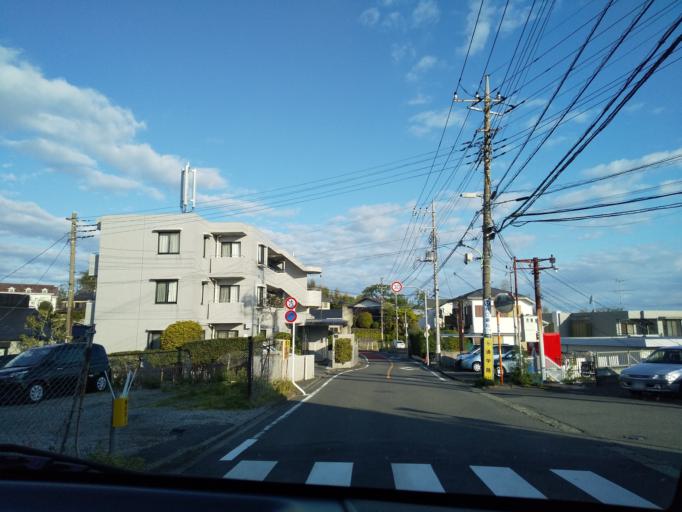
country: JP
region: Tokyo
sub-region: Machida-shi
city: Machida
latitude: 35.5684
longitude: 139.4591
